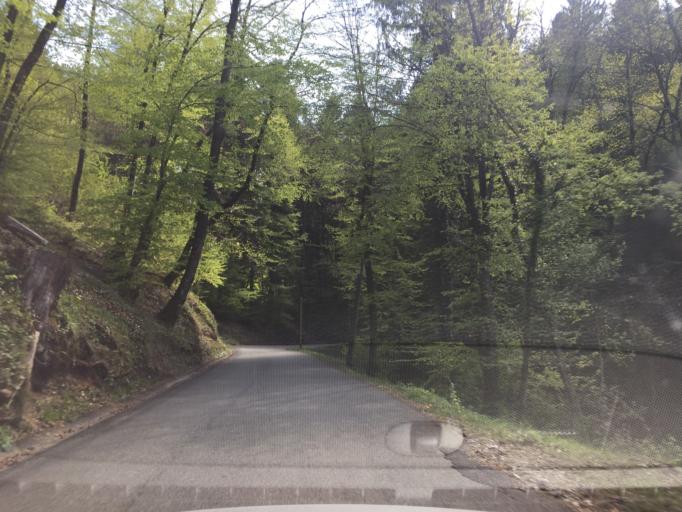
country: FR
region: Rhone-Alpes
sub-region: Departement de la Savoie
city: Vimines
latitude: 45.5704
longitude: 5.8367
